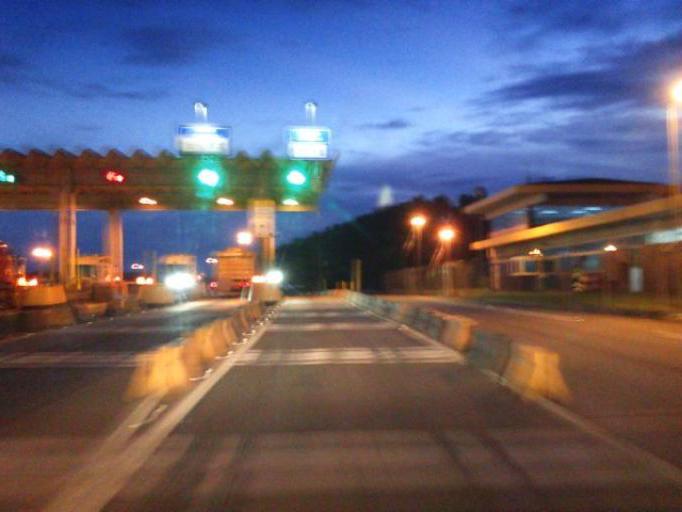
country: BR
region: Santa Catarina
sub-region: Barra Velha
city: Barra Velha
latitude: -26.5913
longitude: -48.7225
